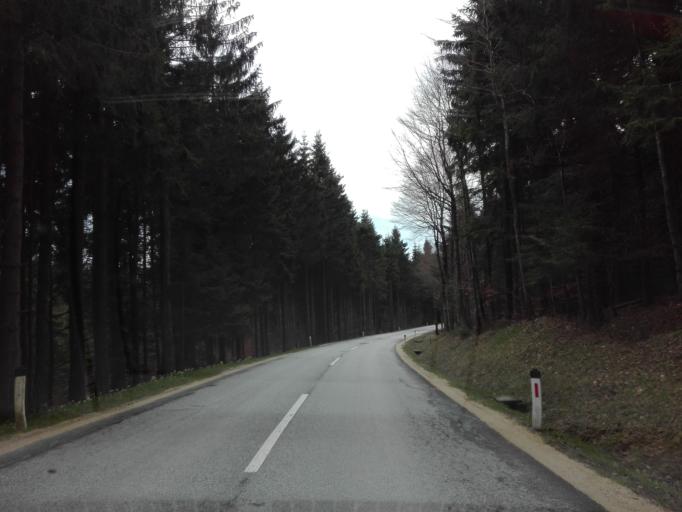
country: AT
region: Upper Austria
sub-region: Politischer Bezirk Rohrbach
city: Ulrichsberg
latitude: 48.7032
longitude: 13.9427
